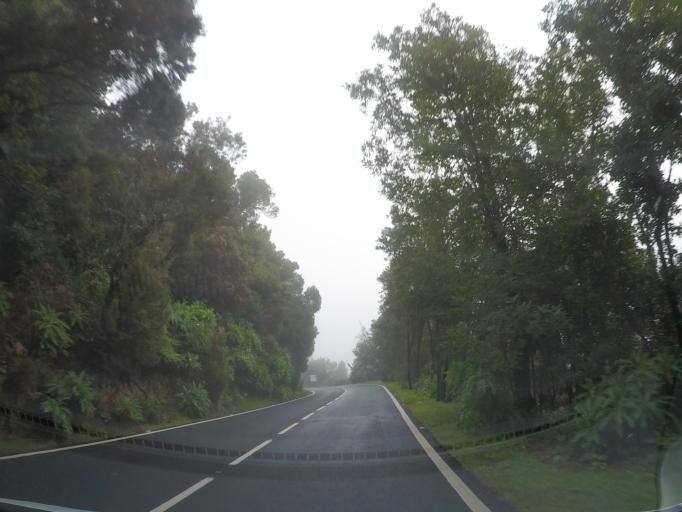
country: ES
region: Canary Islands
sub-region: Provincia de Santa Cruz de Tenerife
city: Alajero
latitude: 28.1181
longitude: -17.2466
